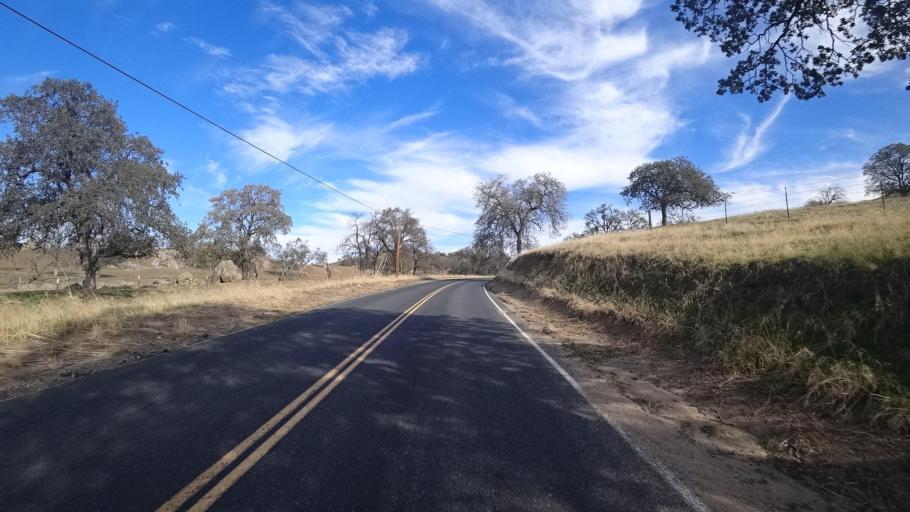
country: US
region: California
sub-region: Kern County
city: Oildale
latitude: 35.6252
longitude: -118.8423
